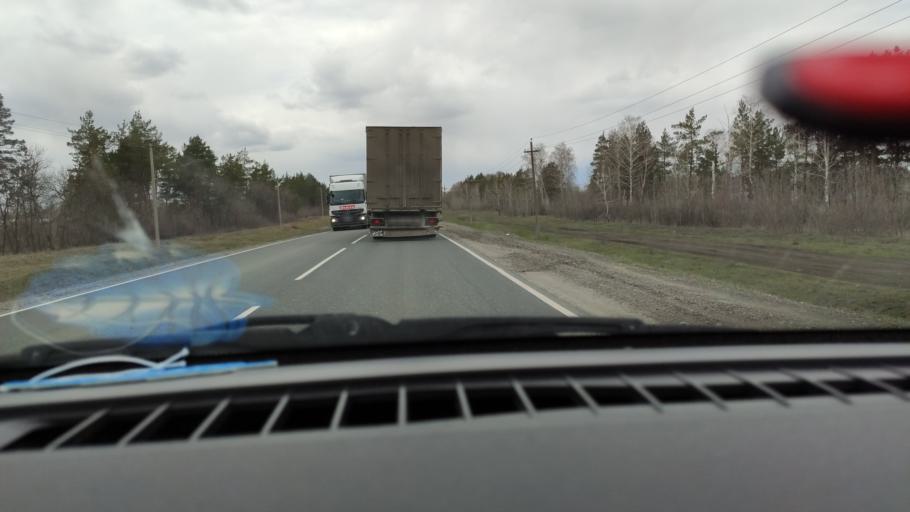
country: RU
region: Saratov
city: Sennoy
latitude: 52.1520
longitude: 46.9668
